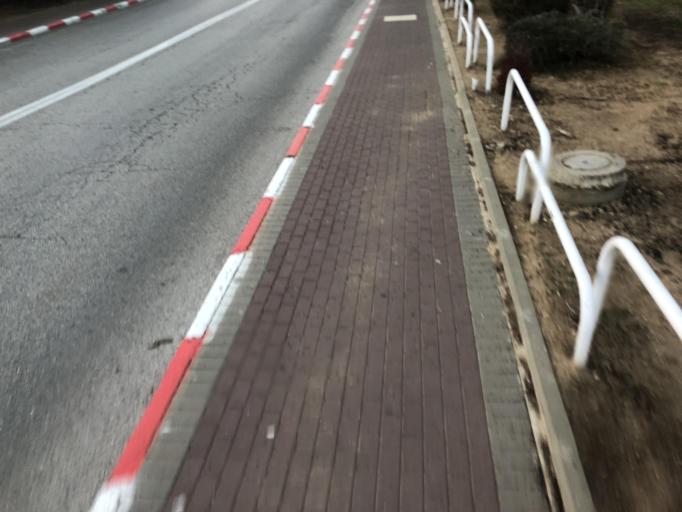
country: IL
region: Northern District
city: `Akko
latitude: 32.9326
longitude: 35.0925
